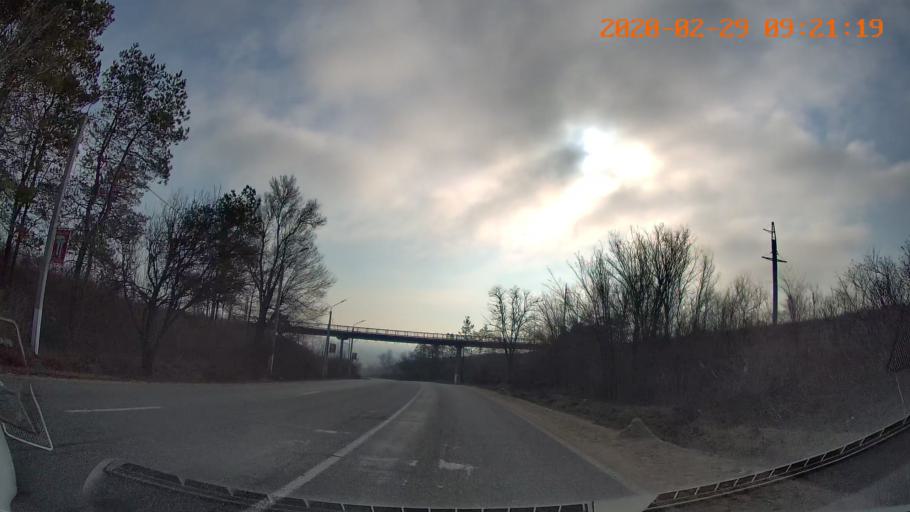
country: MD
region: Telenesti
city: Pervomaisc
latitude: 46.7391
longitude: 29.9570
